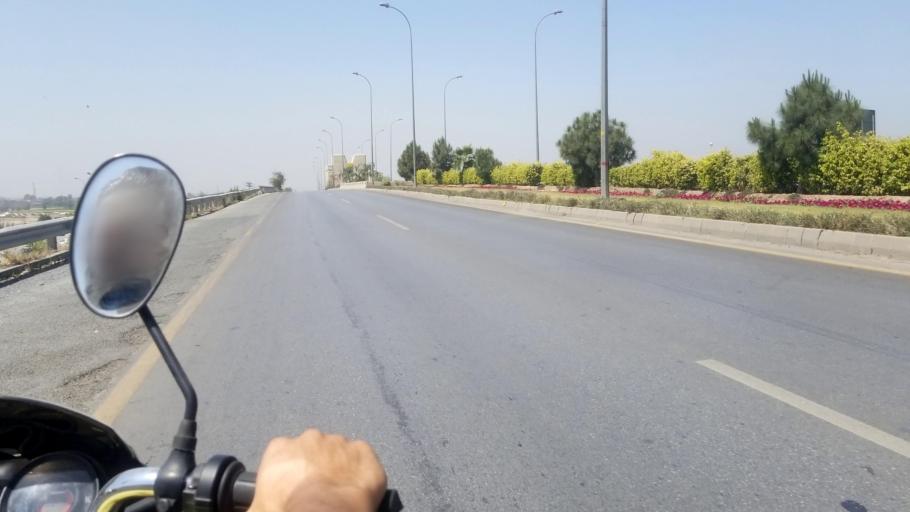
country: PK
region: Khyber Pakhtunkhwa
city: Peshawar
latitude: 34.0266
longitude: 71.6465
